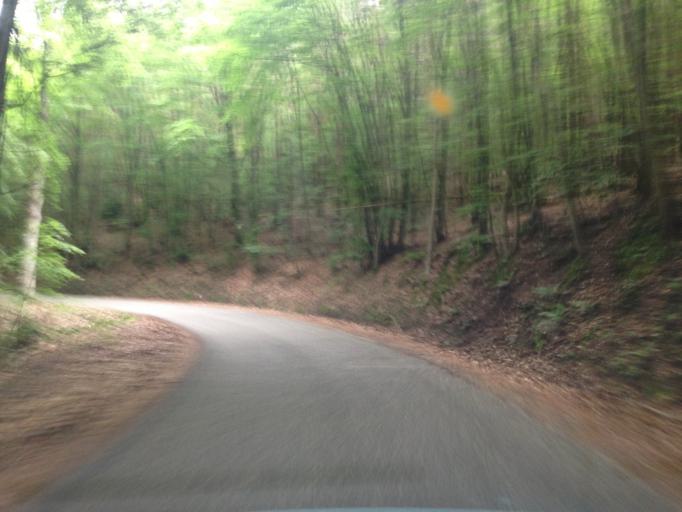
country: FR
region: Alsace
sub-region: Departement du Bas-Rhin
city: Neuwiller-les-Saverne
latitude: 48.8371
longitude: 7.3878
